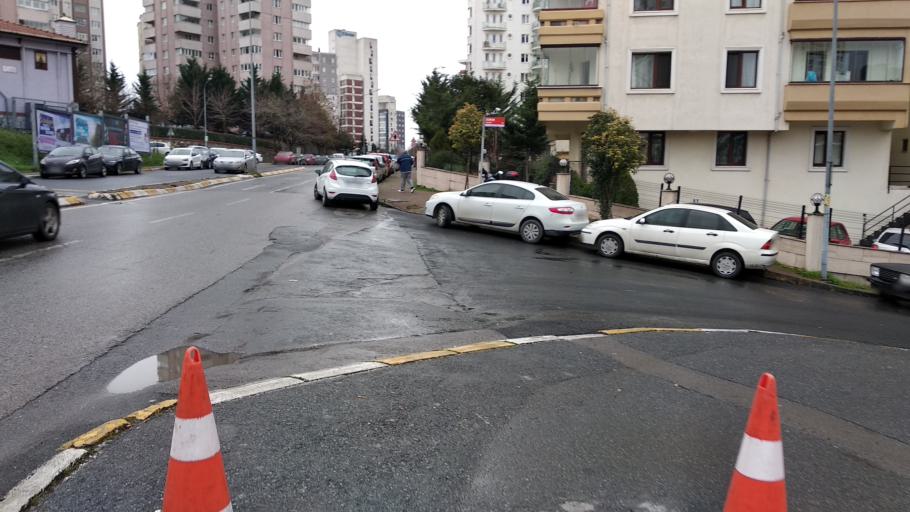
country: TR
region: Istanbul
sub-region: Atasehir
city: Atasehir
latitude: 40.9874
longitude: 29.1241
